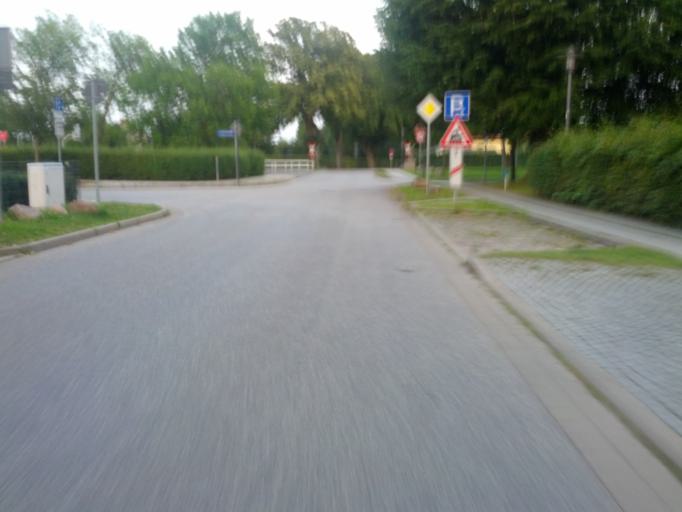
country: DE
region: Mecklenburg-Vorpommern
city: Ostseebad Kuhlungsborn
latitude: 54.1456
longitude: 11.7575
